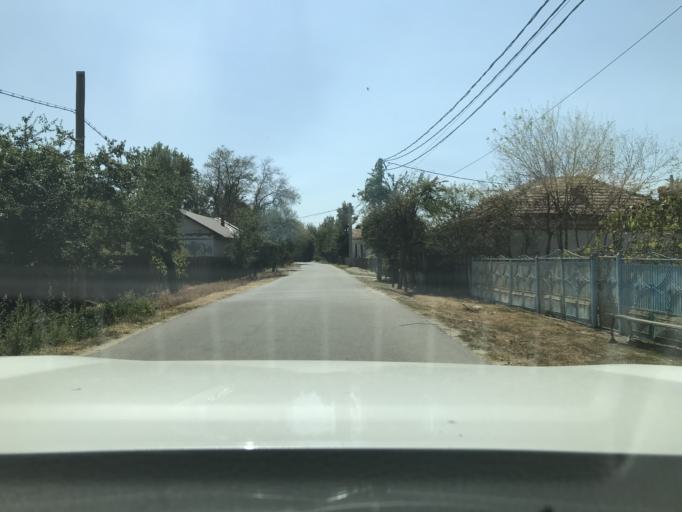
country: RO
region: Olt
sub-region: Comuna Falcoiu
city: Falcoiu
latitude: 44.2433
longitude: 24.3667
